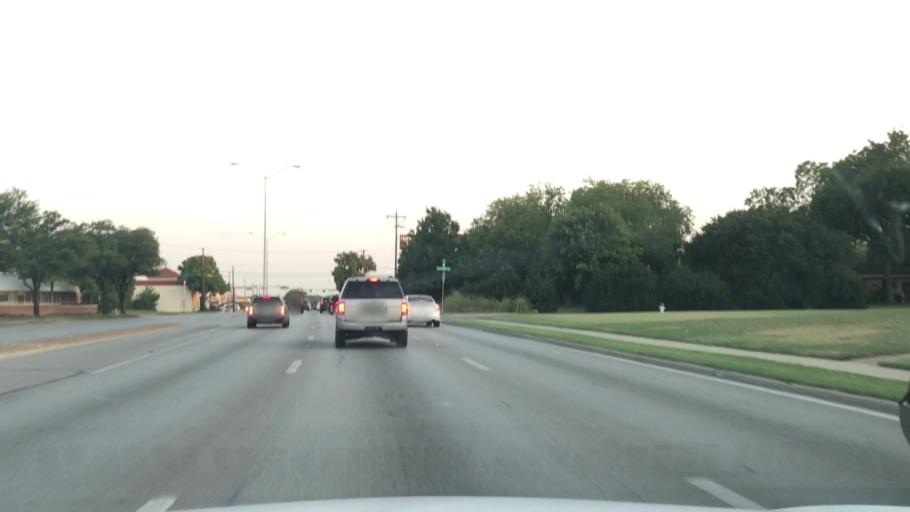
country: US
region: Texas
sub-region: Dallas County
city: Highland Park
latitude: 32.8311
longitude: -96.6990
